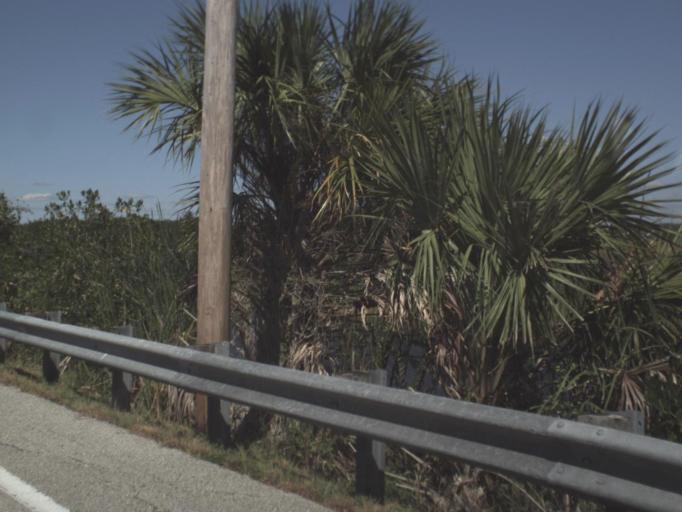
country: US
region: Florida
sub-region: Collier County
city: Marco
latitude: 25.9358
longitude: -81.4544
